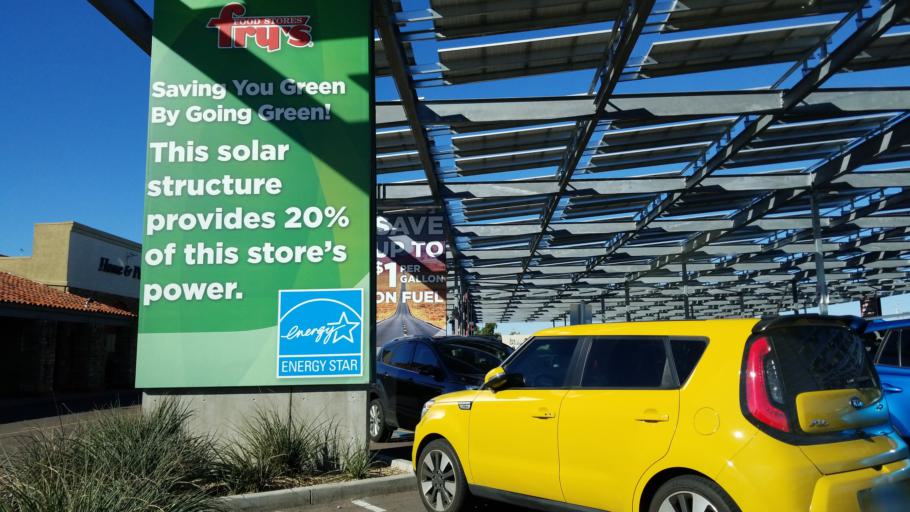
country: US
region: Arizona
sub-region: Maricopa County
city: Glendale
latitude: 33.6387
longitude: -112.1193
